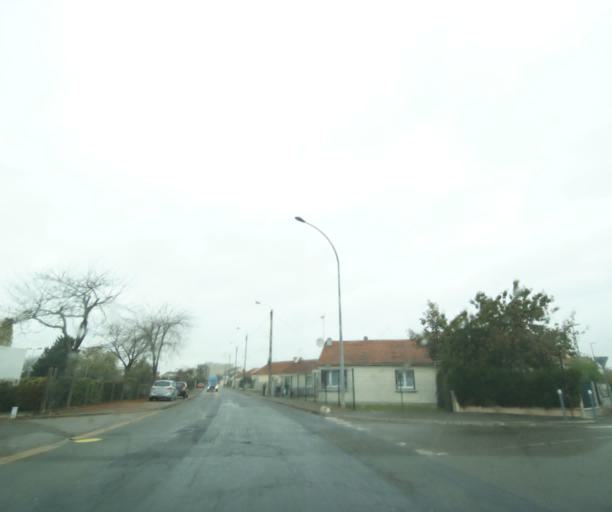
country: FR
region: Centre
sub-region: Departement d'Eure-et-Loir
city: Vernouillet
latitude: 48.7223
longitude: 1.3727
